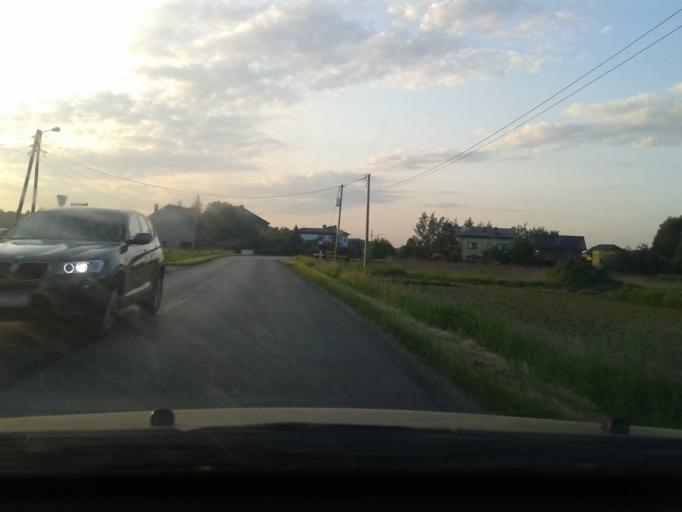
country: PL
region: Lesser Poland Voivodeship
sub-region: Powiat oswiecimski
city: Przecieszyn
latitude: 49.9471
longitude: 19.1838
